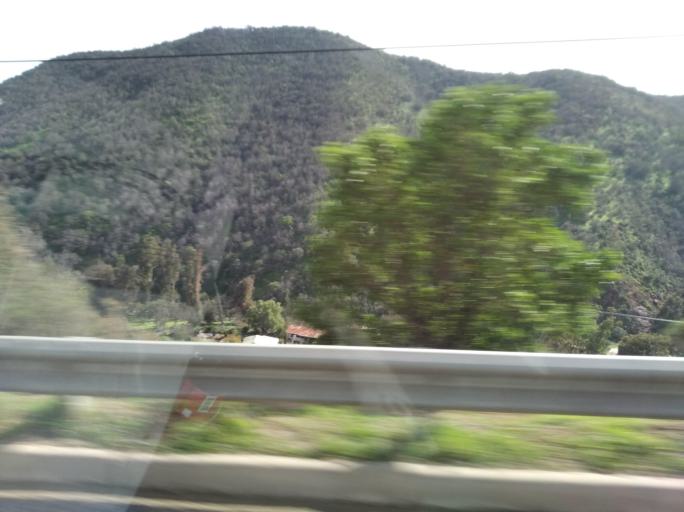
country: CL
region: Valparaiso
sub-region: Provincia de Marga Marga
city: Limache
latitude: -33.0628
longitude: -71.0621
